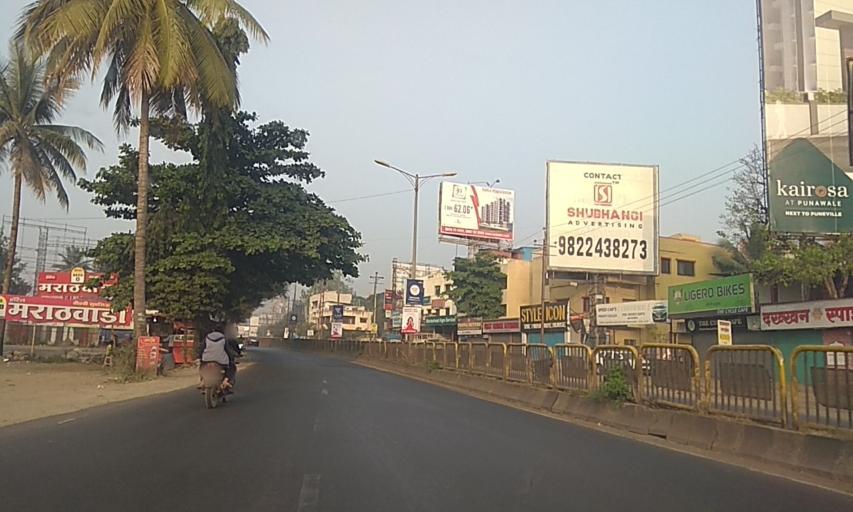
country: IN
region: Maharashtra
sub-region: Pune Division
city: Pimpri
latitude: 18.5920
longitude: 73.7652
